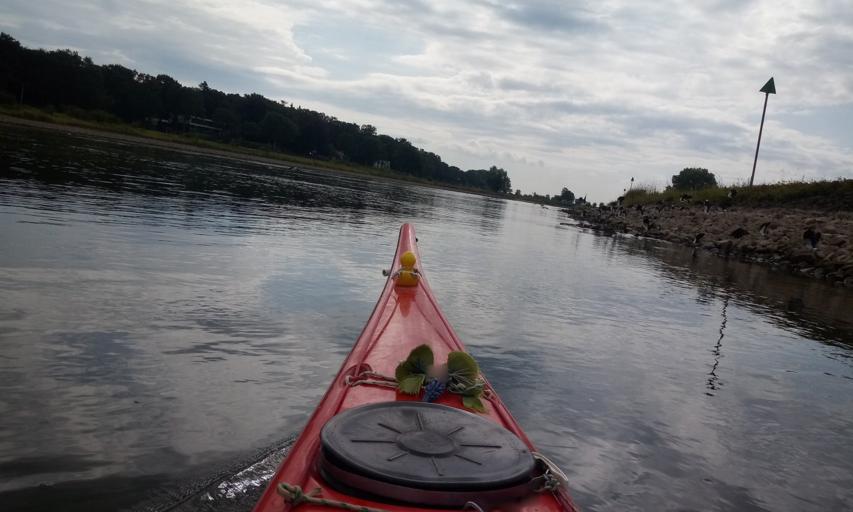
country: NL
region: Gelderland
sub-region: Gemeente Lochem
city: Gorssel
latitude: 52.2077
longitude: 6.1886
